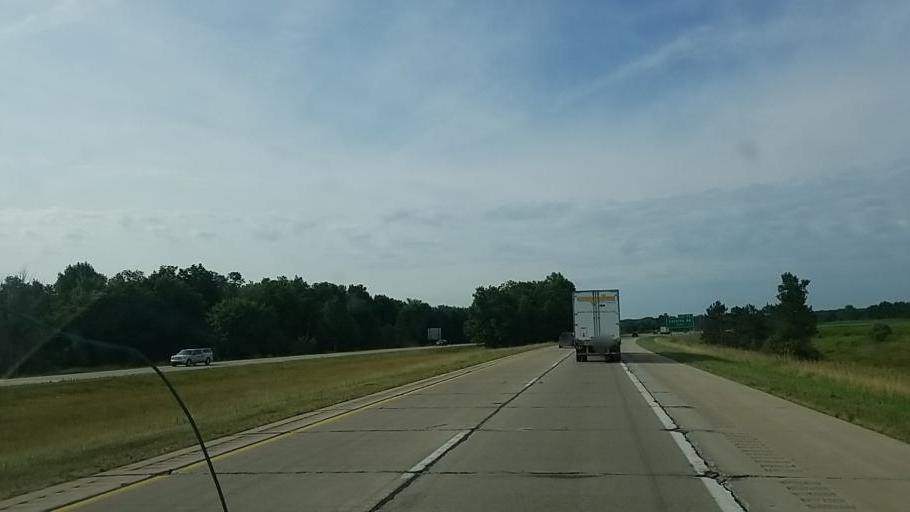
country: US
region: Michigan
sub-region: Eaton County
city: Charlotte
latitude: 42.5334
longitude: -84.8214
